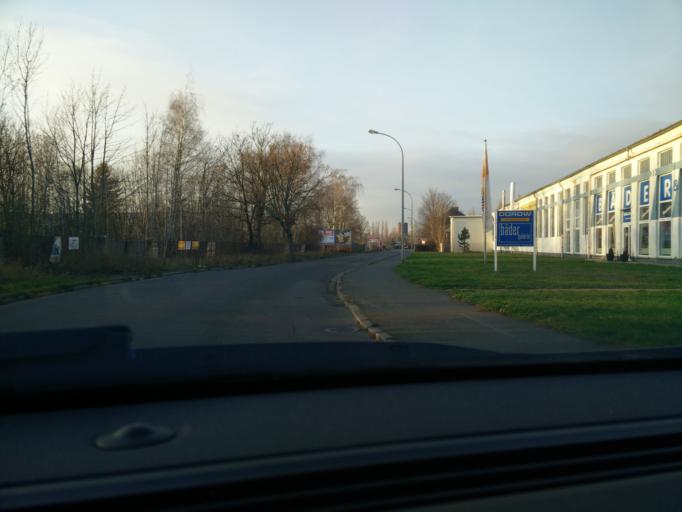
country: DE
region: Saxony
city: Taucha
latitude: 51.3367
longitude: 12.4713
